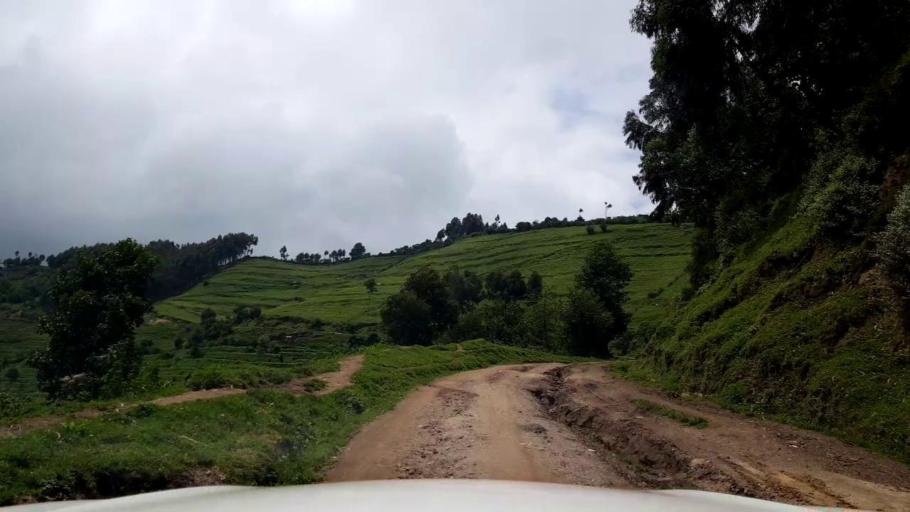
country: RW
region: Western Province
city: Gisenyi
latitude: -1.6678
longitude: 29.4118
